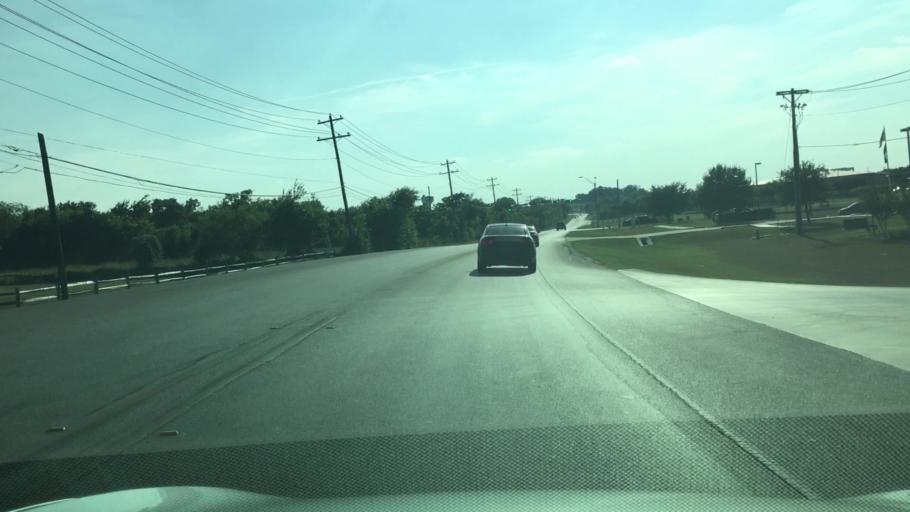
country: US
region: Texas
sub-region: Hays County
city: Buda
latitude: 30.0965
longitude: -97.8781
